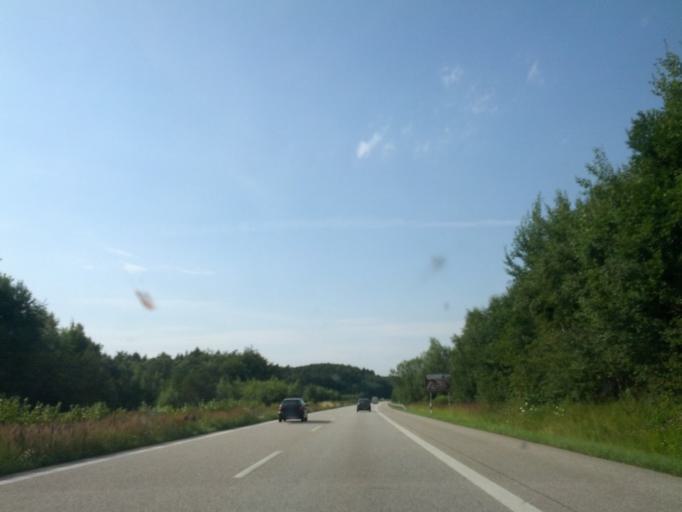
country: DE
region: Mecklenburg-Vorpommern
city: Lalendorf
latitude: 53.7386
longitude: 12.3398
